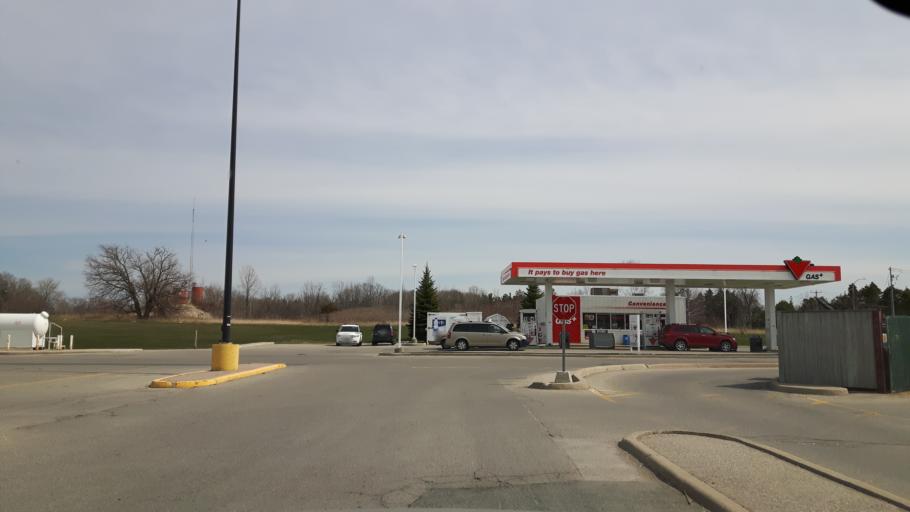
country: CA
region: Ontario
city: Goderich
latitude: 43.7302
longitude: -81.6881
